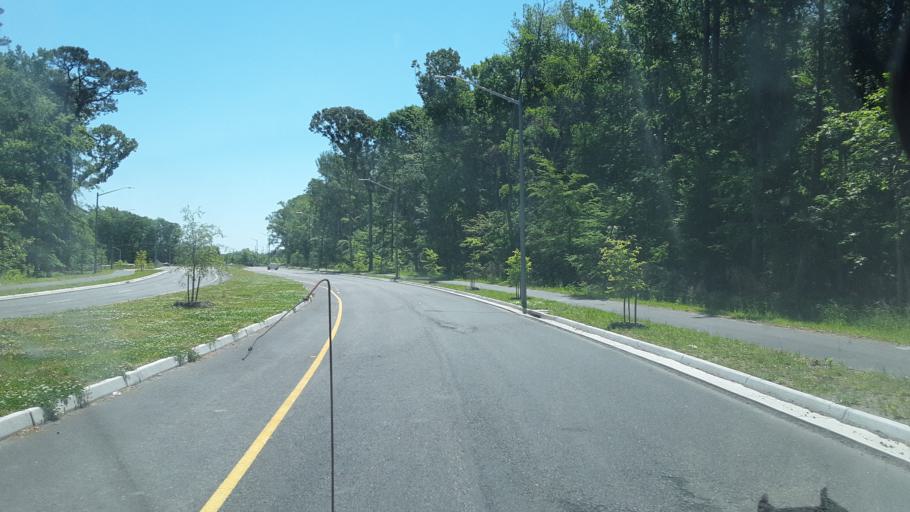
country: US
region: Virginia
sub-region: City of Virginia Beach
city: Virginia Beach
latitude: 36.7593
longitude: -76.0177
